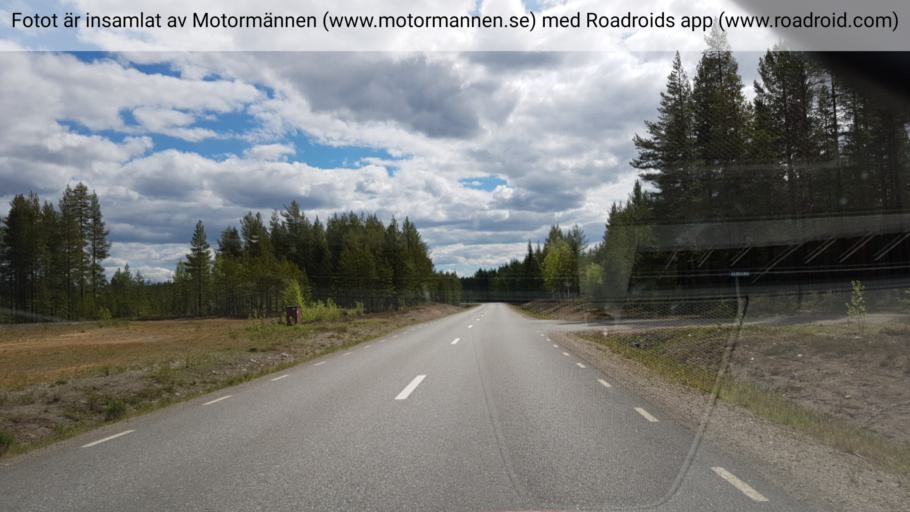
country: SE
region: Vaesterbotten
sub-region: Skelleftea Kommun
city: Langsele
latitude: 64.8068
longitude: 19.9980
